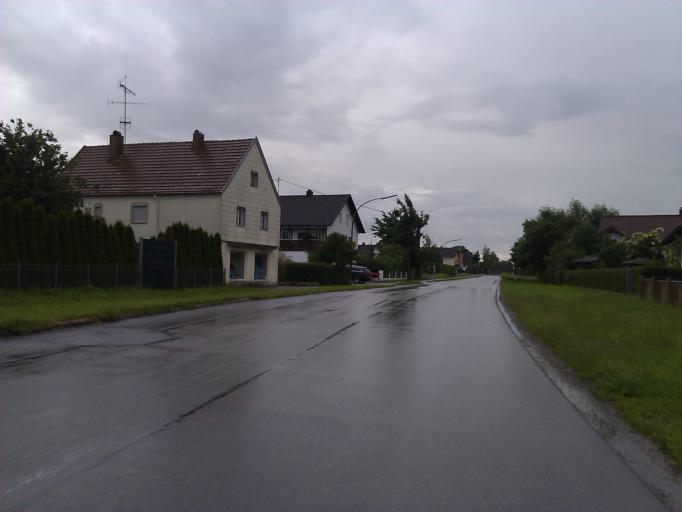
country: DE
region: Bavaria
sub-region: Swabia
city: Tussenhausen
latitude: 48.0635
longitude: 10.5826
